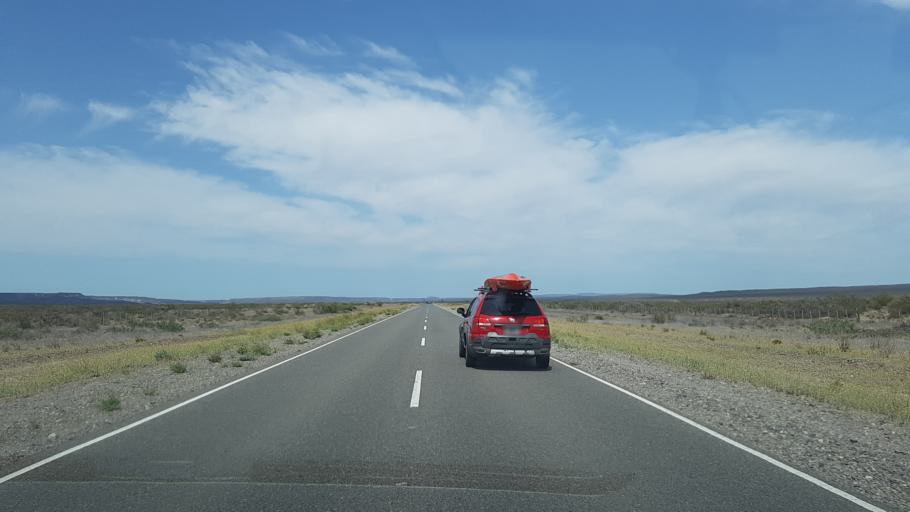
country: AR
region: Neuquen
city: Piedra del Aguila
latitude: -39.8639
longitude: -69.8252
